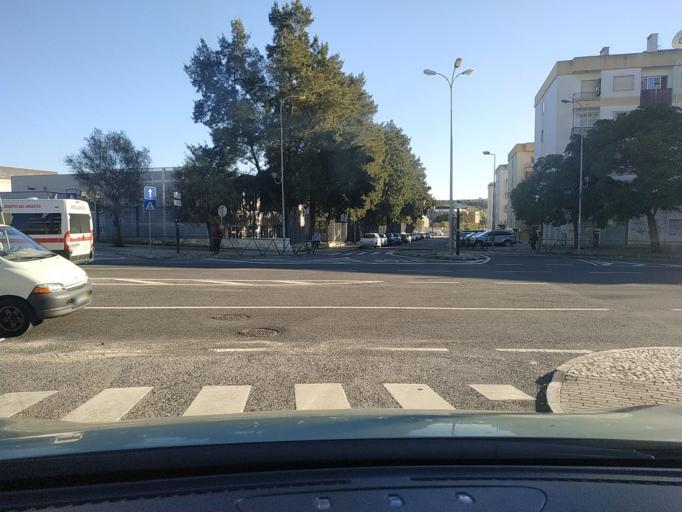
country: PT
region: Lisbon
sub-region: Sintra
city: Queluz
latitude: 38.7607
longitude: -9.2484
